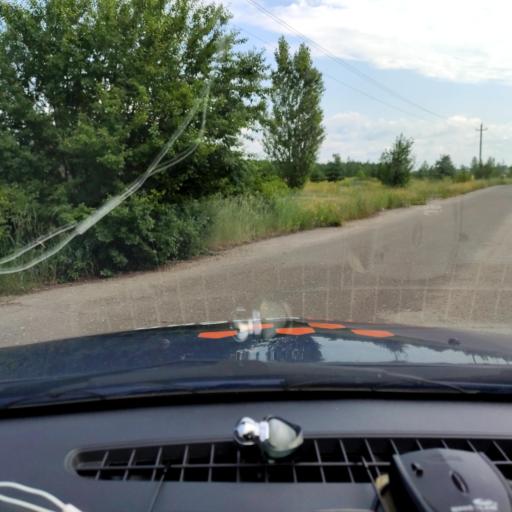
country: RU
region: Voronezj
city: Ramon'
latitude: 52.0758
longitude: 39.3090
